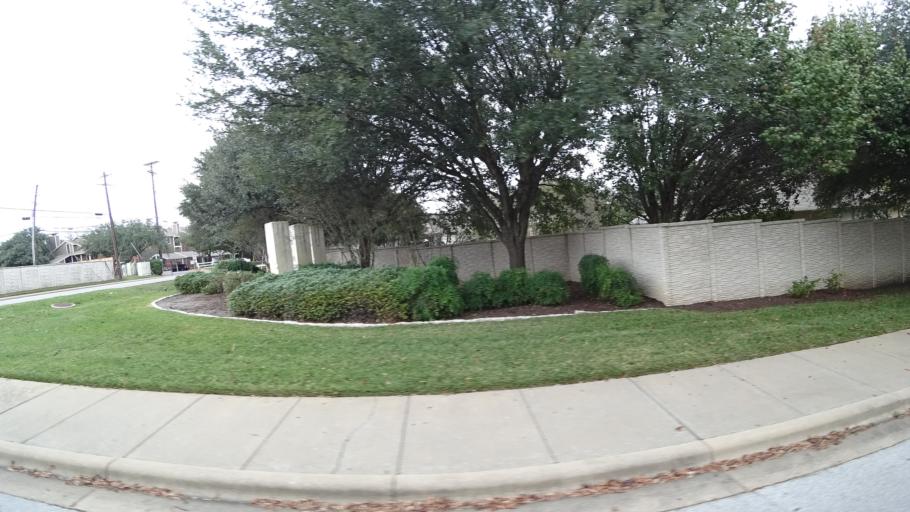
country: US
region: Texas
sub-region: Travis County
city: Wells Branch
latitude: 30.4514
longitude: -97.6823
